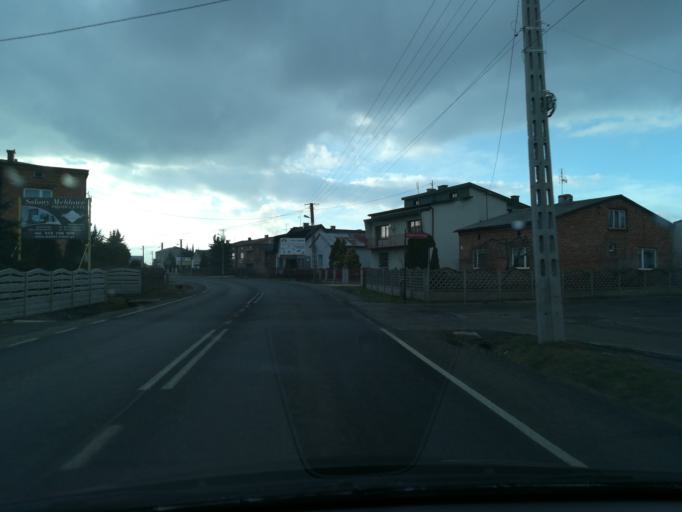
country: PL
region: Lodz Voivodeship
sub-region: Powiat radomszczanski
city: Radomsko
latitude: 51.0772
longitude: 19.3975
